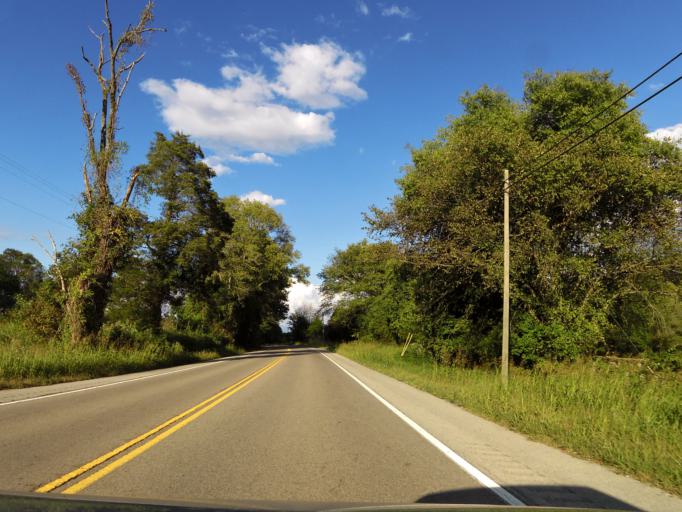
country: US
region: Tennessee
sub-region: Grainger County
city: Blaine
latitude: 36.2143
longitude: -83.6457
